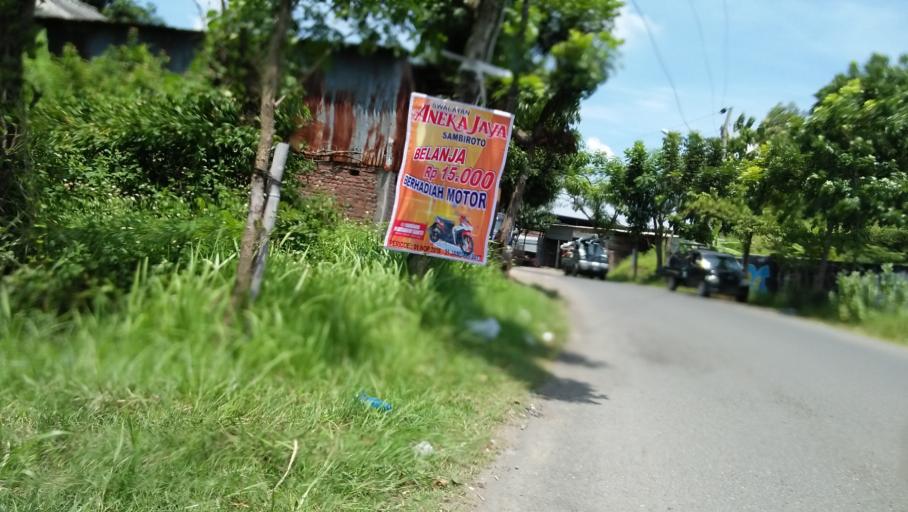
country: ID
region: Central Java
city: Mranggen
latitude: -7.0402
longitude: 110.4659
